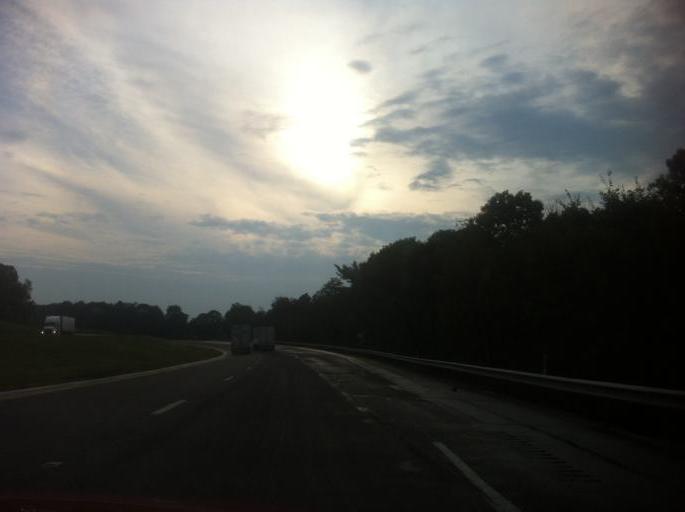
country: US
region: Pennsylvania
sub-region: Clarion County
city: Knox
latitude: 41.1860
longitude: -79.6667
